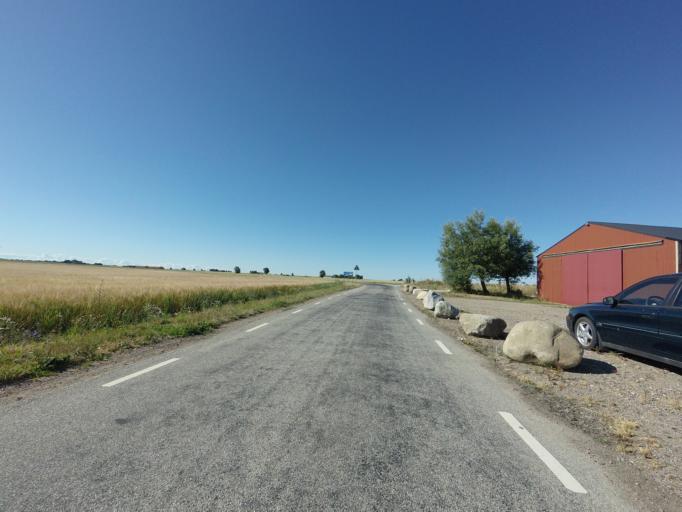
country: SE
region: Skane
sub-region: Trelleborgs Kommun
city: Skare
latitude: 55.3999
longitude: 13.0184
